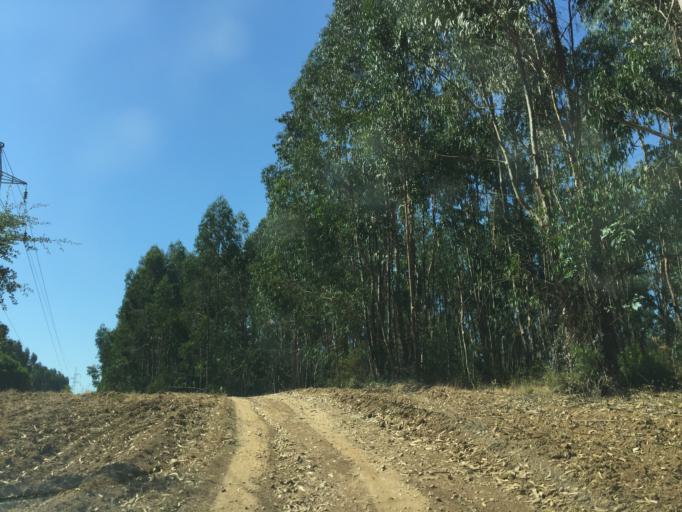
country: PT
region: Santarem
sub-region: Tomar
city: Tomar
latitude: 39.6121
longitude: -8.3570
